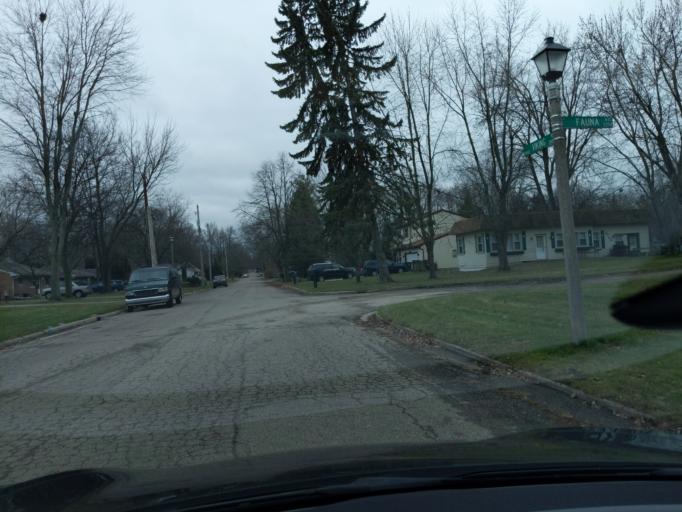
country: US
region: Michigan
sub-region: Ingham County
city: Lansing
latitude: 42.7032
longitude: -84.5872
